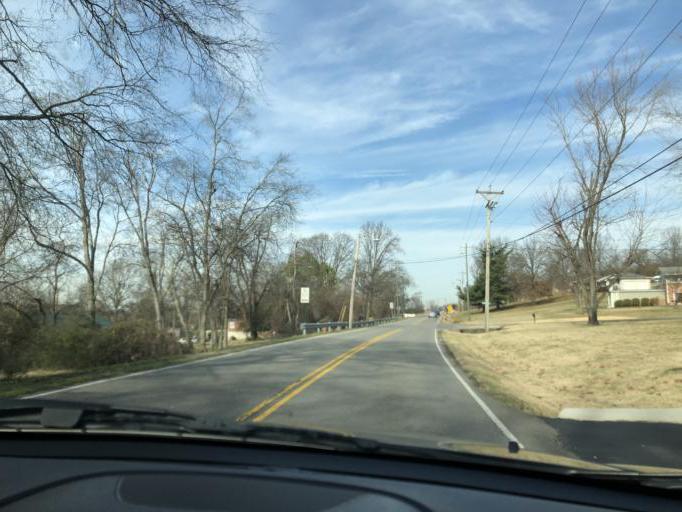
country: US
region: Tennessee
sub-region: Davidson County
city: Lakewood
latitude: 36.2106
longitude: -86.6866
